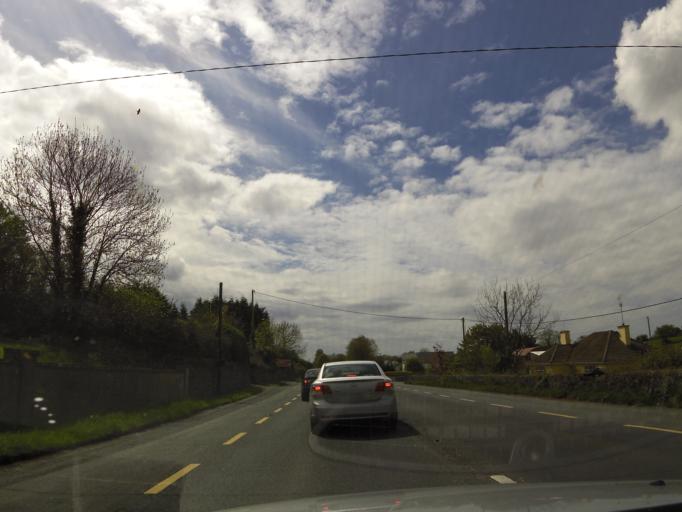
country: IE
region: Connaught
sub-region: County Galway
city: Gaillimh
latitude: 53.3058
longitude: -8.9992
